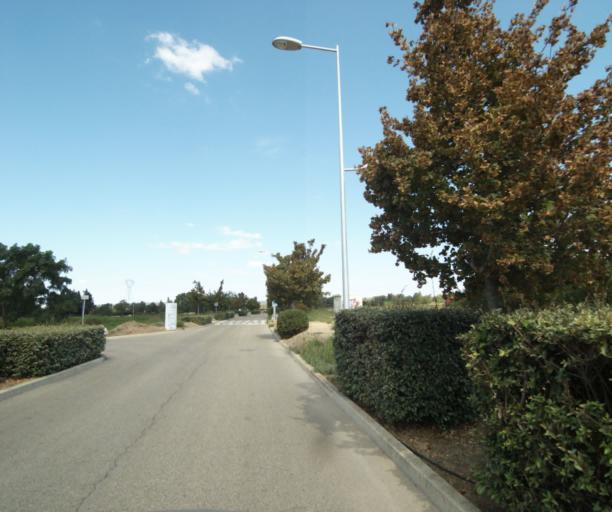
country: FR
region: Languedoc-Roussillon
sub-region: Departement du Gard
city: Bouillargues
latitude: 43.8095
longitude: 4.4112
